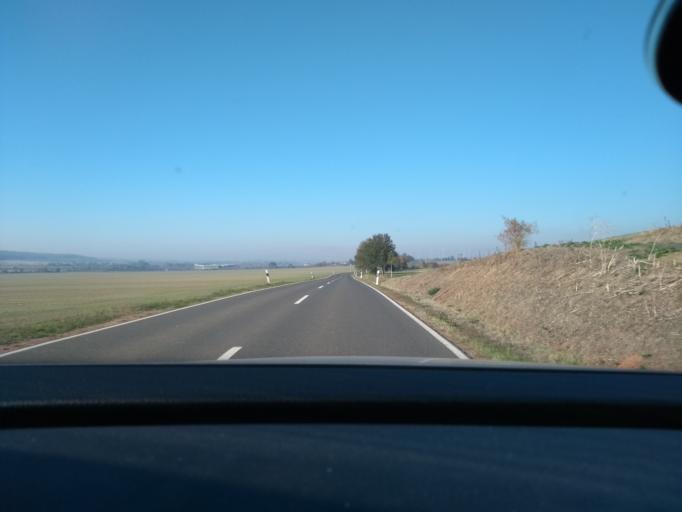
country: DE
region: Saxony-Anhalt
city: Farnstadt
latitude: 51.4525
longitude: 11.5674
